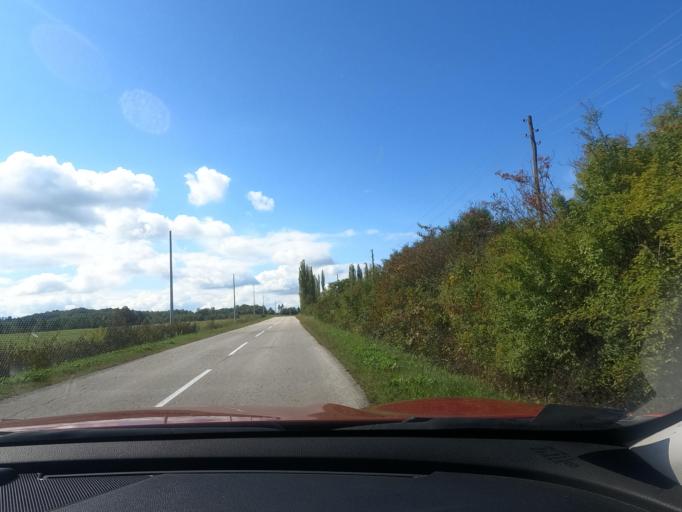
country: BA
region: Federation of Bosnia and Herzegovina
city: Vrnograc
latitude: 45.2394
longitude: 15.9388
